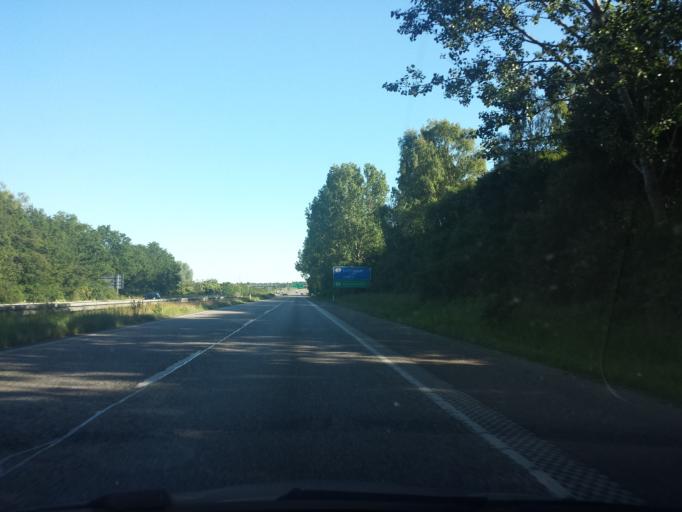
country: DK
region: Capital Region
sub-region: Ballerup Kommune
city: Ballerup
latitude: 55.7148
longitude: 12.3656
